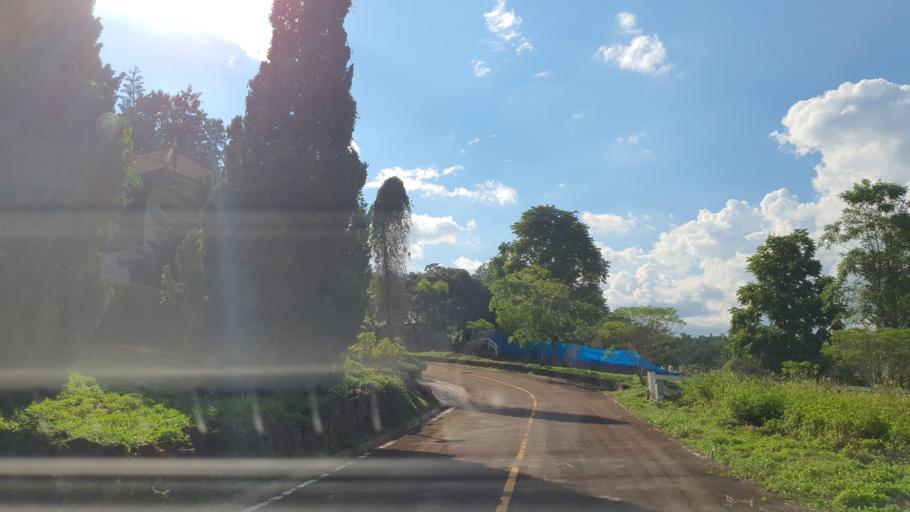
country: TH
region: Chiang Mai
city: Hang Dong
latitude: 18.7647
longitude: 98.8678
